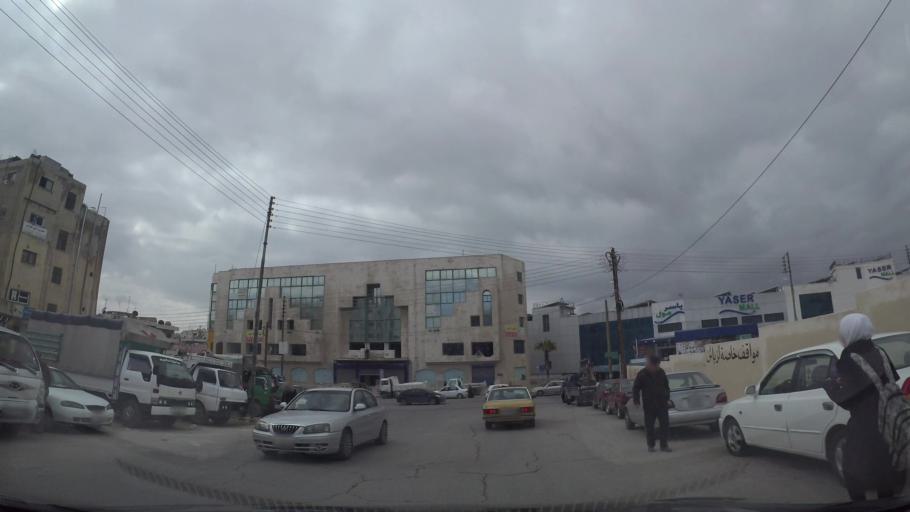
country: JO
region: Amman
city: Wadi as Sir
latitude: 31.9549
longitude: 35.8352
